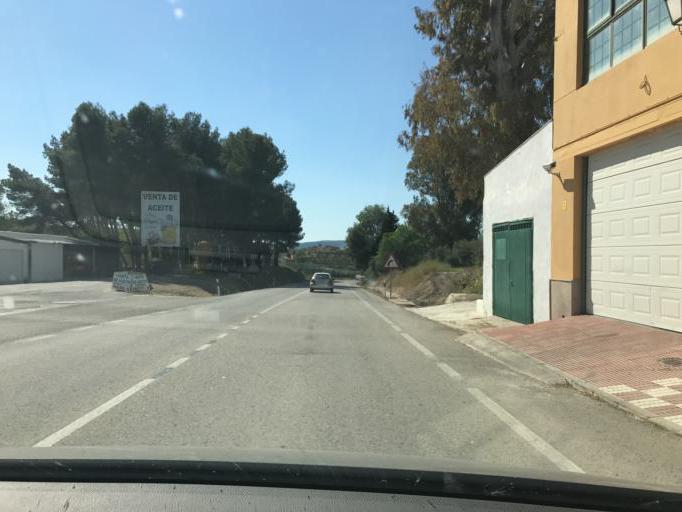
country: ES
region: Andalusia
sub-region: Province of Cordoba
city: Luque
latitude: 37.5733
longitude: -4.2624
